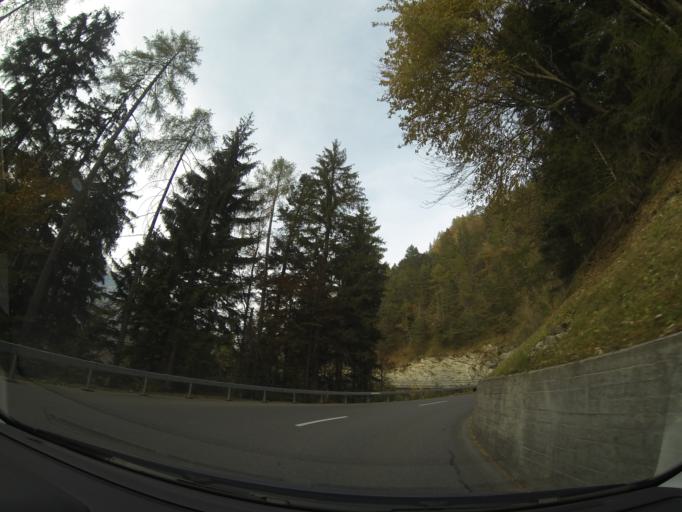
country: CH
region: Grisons
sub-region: Landquart District
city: Untervaz
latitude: 46.9494
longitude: 9.4842
